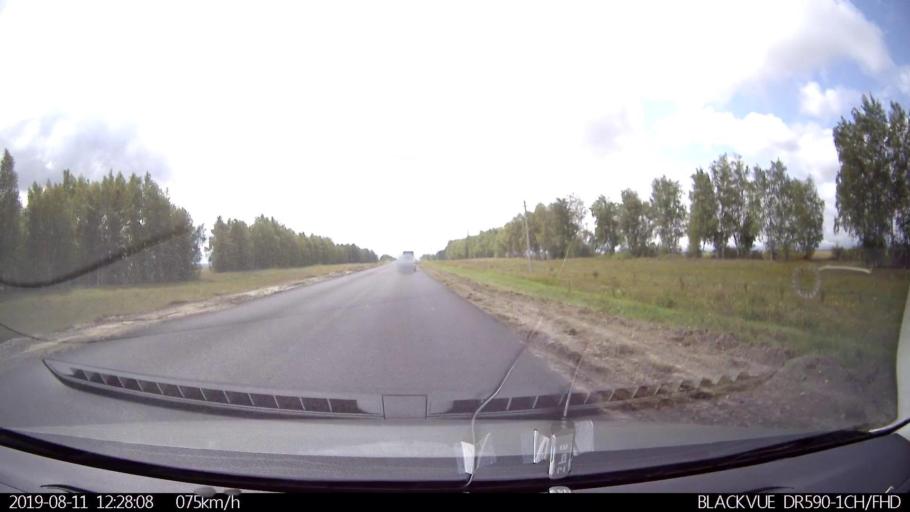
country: RU
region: Ulyanovsk
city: Ignatovka
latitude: 53.8469
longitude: 47.9142
